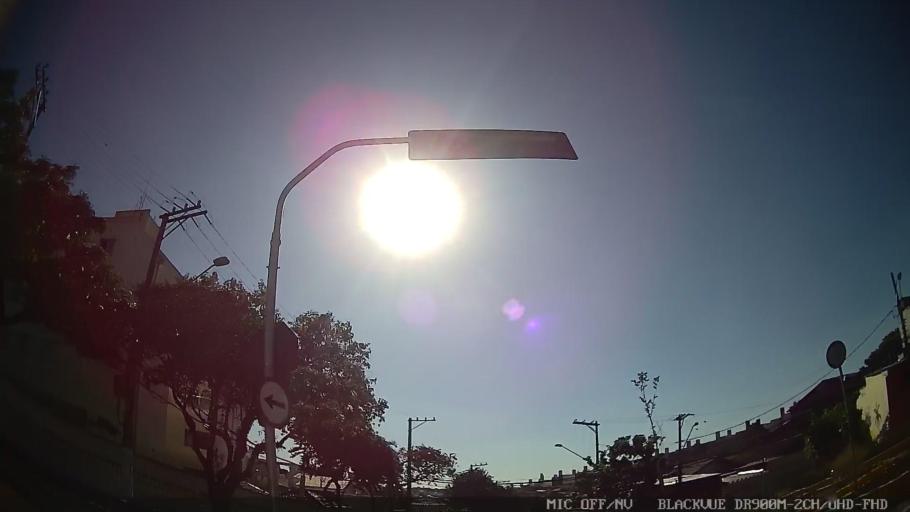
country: BR
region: Sao Paulo
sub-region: Sao Caetano Do Sul
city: Sao Caetano do Sul
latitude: -23.5529
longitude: -46.4843
